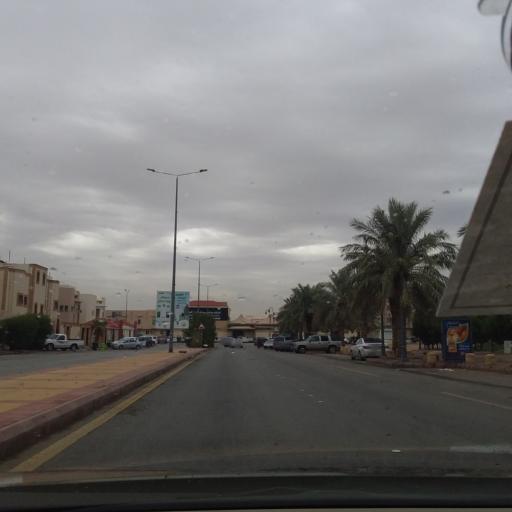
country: SA
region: Ar Riyad
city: Riyadh
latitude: 24.7322
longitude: 46.7767
